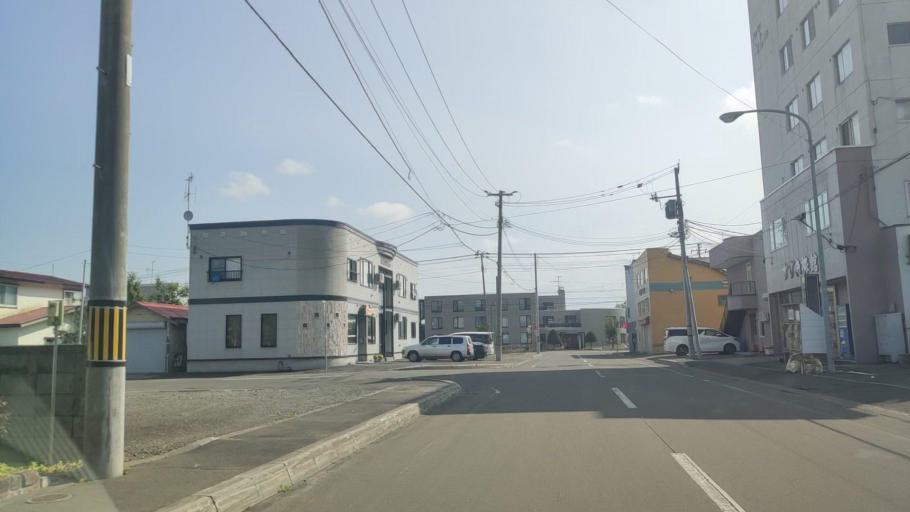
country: JP
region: Hokkaido
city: Shimo-furano
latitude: 43.3440
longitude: 142.3912
